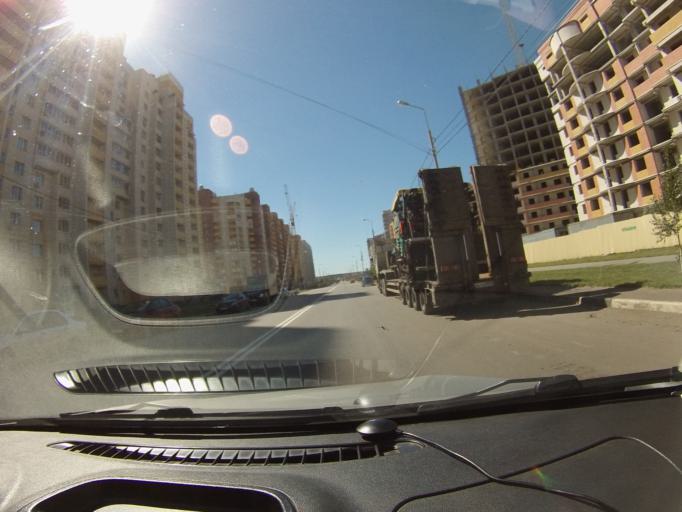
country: RU
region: Tambov
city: Tambov
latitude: 52.7727
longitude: 41.4007
